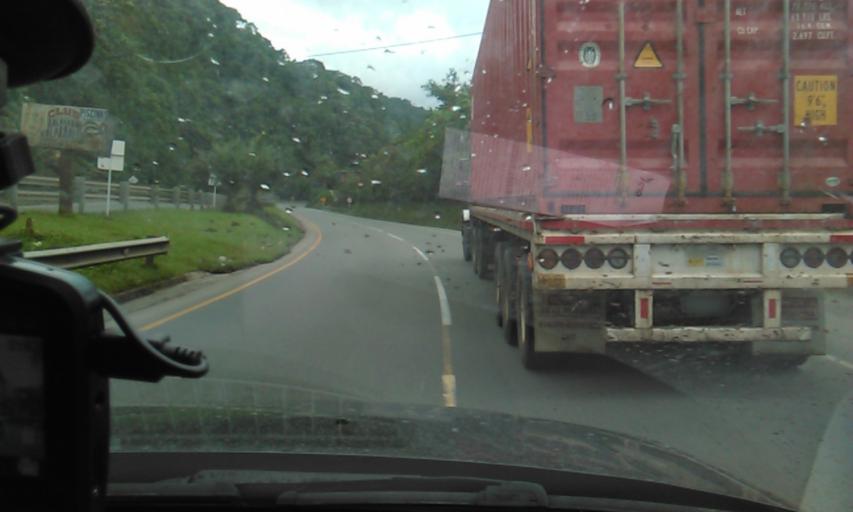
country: CO
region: Valle del Cauca
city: Dagua
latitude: 3.8486
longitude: -76.7978
